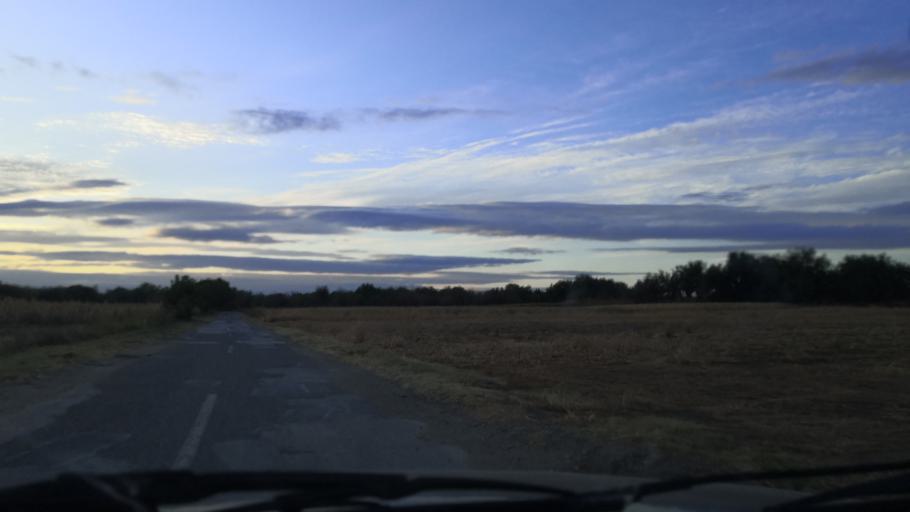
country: RO
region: Mehedinti
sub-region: Comuna Gruia
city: Izvoarele
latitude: 44.2731
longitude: 22.6652
